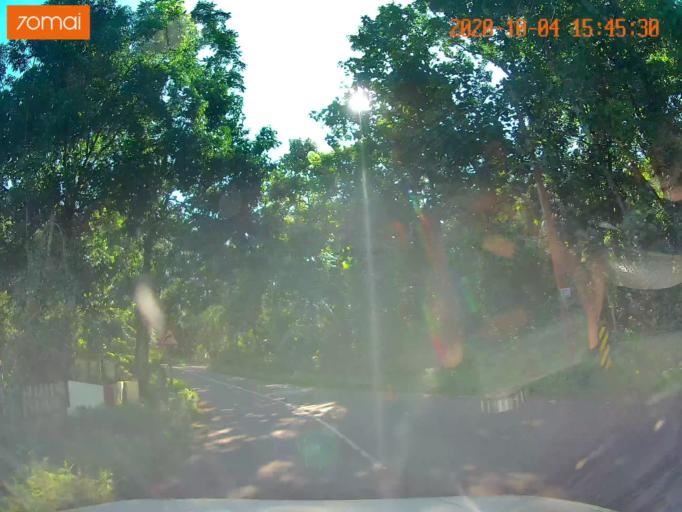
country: IN
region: Kerala
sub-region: Kottayam
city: Palackattumala
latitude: 9.7606
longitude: 76.5800
